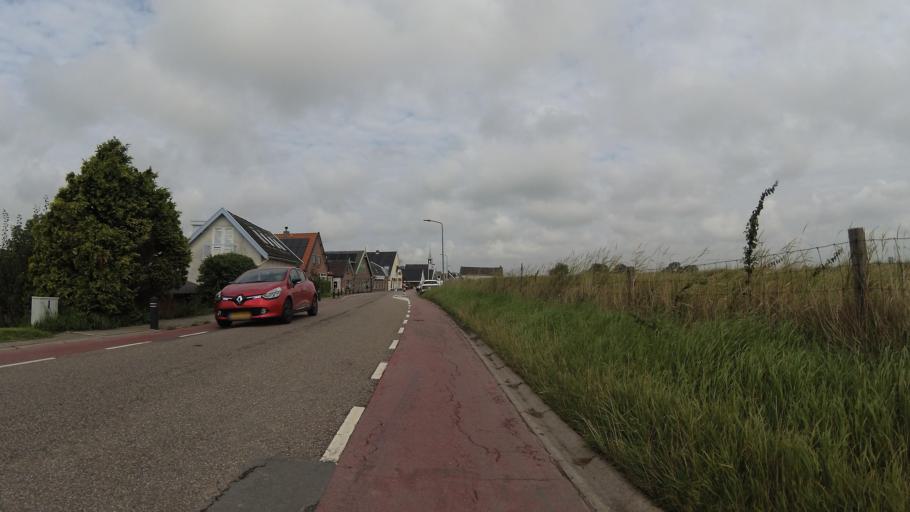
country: NL
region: North Holland
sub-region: Gemeente Schagen
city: Schagen
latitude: 52.8326
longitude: 4.8122
